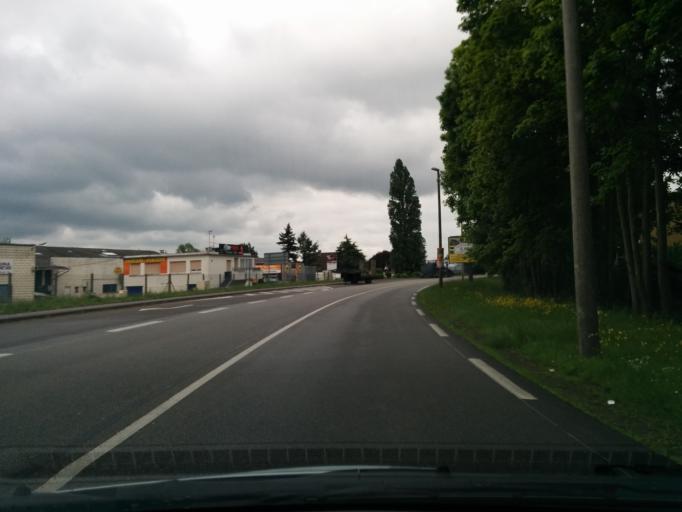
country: FR
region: Haute-Normandie
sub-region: Departement de l'Eure
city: Vernon
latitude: 49.0824
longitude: 1.5032
